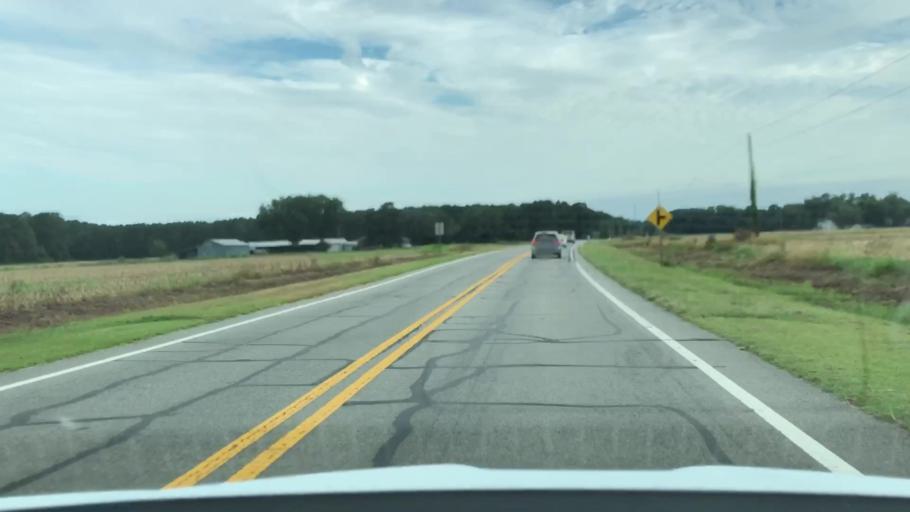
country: US
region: North Carolina
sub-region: Lenoir County
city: Kinston
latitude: 35.1592
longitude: -77.5545
